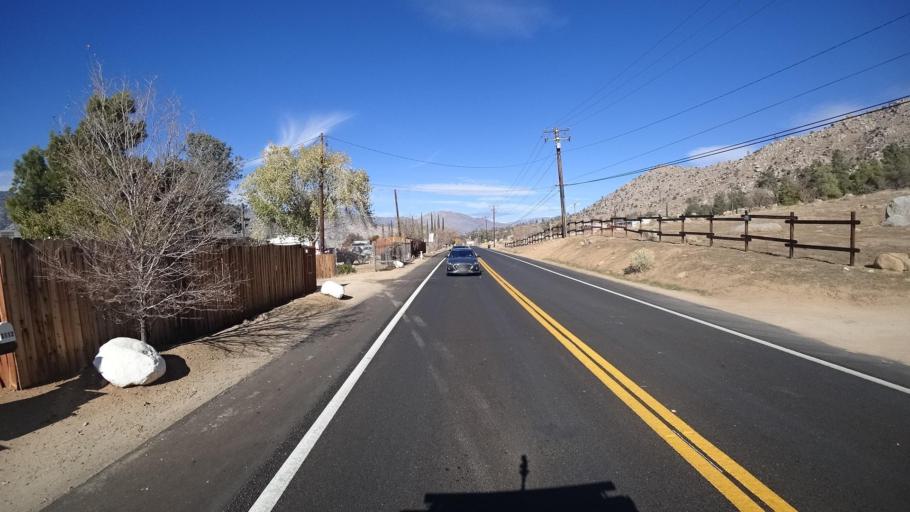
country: US
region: California
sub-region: Kern County
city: Lake Isabella
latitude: 35.6141
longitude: -118.4681
